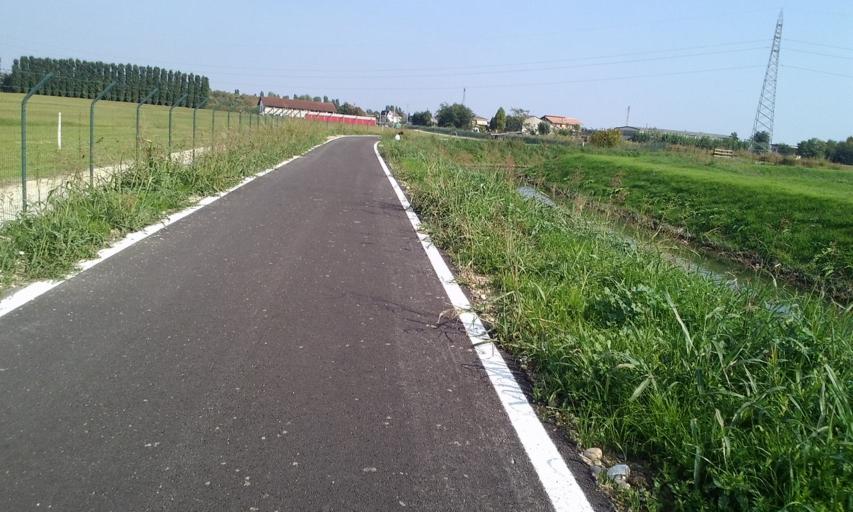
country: IT
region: Veneto
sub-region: Provincia di Verona
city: Buttapietra
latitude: 45.3511
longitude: 10.9889
